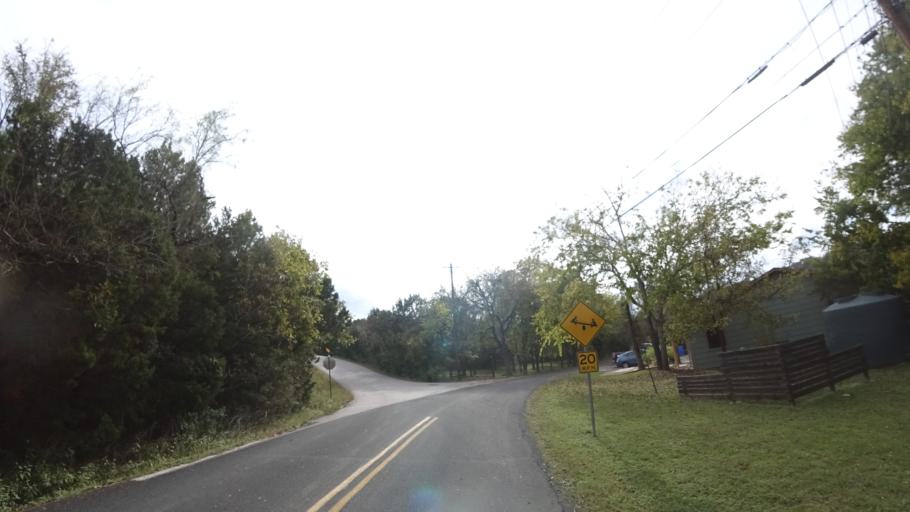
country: US
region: Texas
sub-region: Travis County
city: Hudson Bend
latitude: 30.3831
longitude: -97.9104
